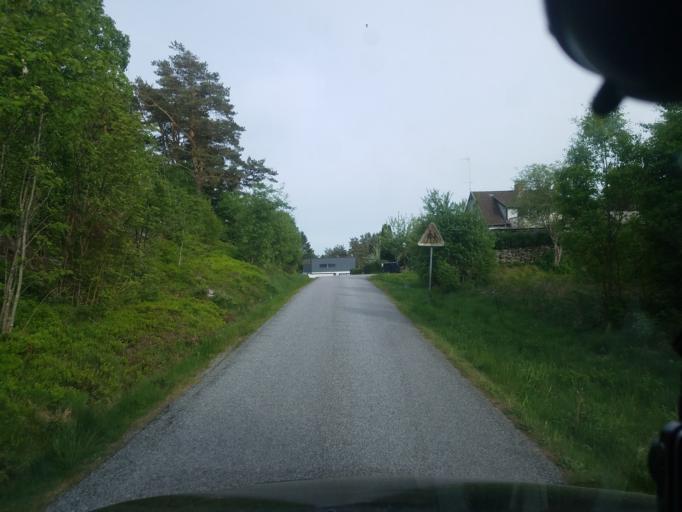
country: SE
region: Vaestra Goetaland
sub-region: Lysekils Kommun
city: Lysekil
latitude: 58.2987
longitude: 11.4705
